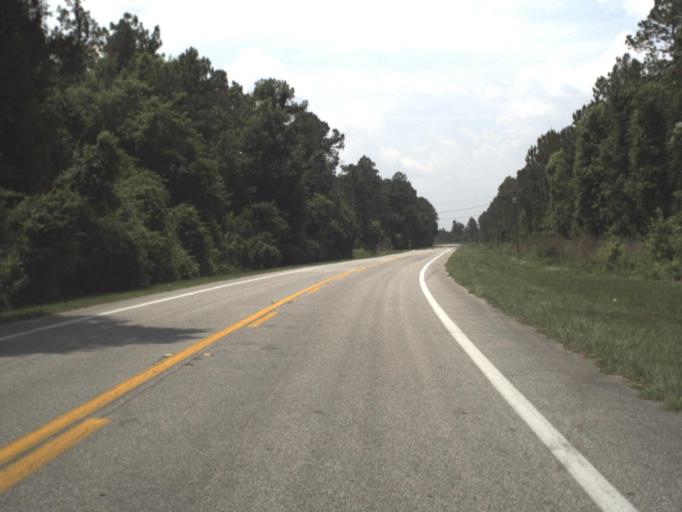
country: US
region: Florida
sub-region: Putnam County
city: Palatka
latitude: 29.5965
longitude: -81.7120
